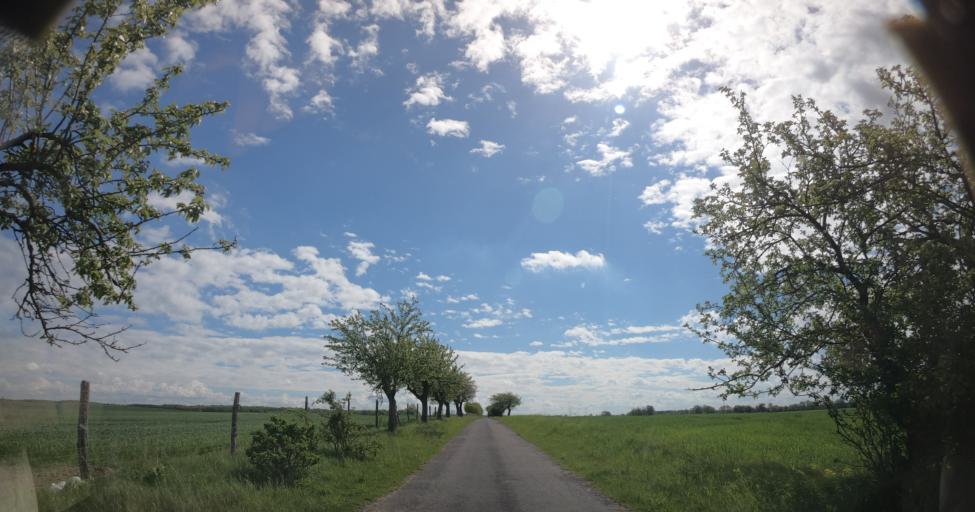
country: PL
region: West Pomeranian Voivodeship
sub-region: Powiat stargardzki
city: Dobrzany
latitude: 53.3522
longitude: 15.4416
